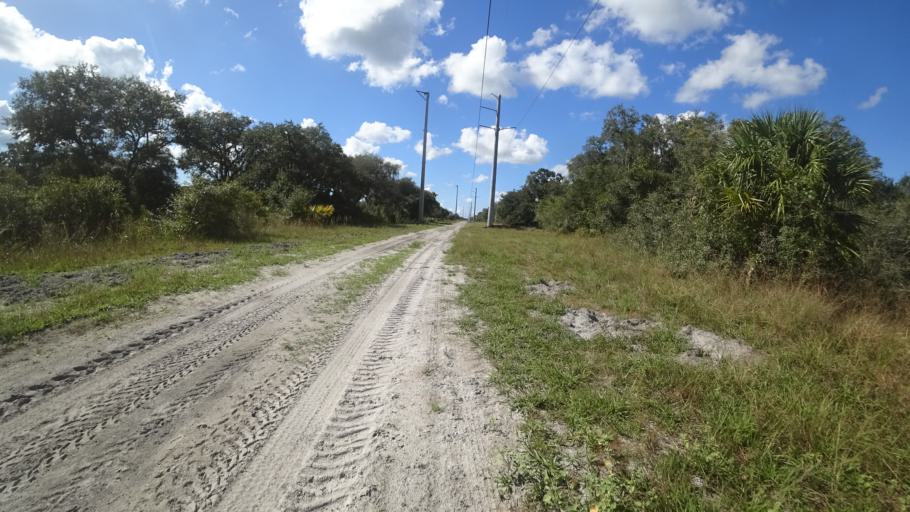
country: US
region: Florida
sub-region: Sarasota County
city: Warm Mineral Springs
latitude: 27.2422
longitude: -82.2617
